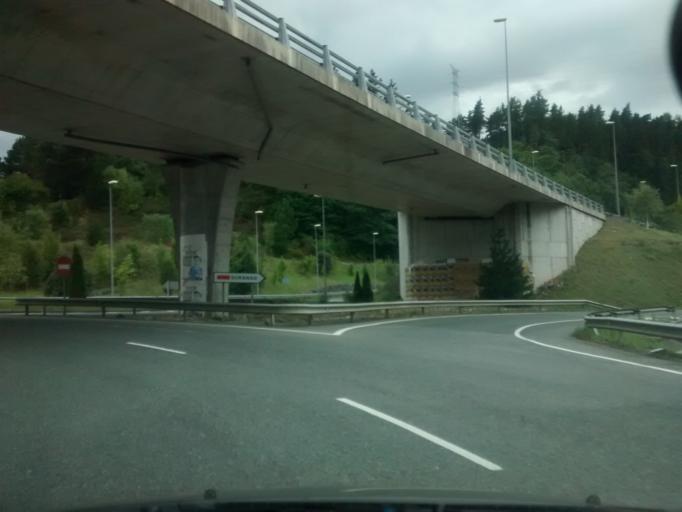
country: ES
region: Basque Country
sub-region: Provincia de Guipuzcoa
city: Arrasate / Mondragon
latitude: 43.0762
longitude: -2.4626
